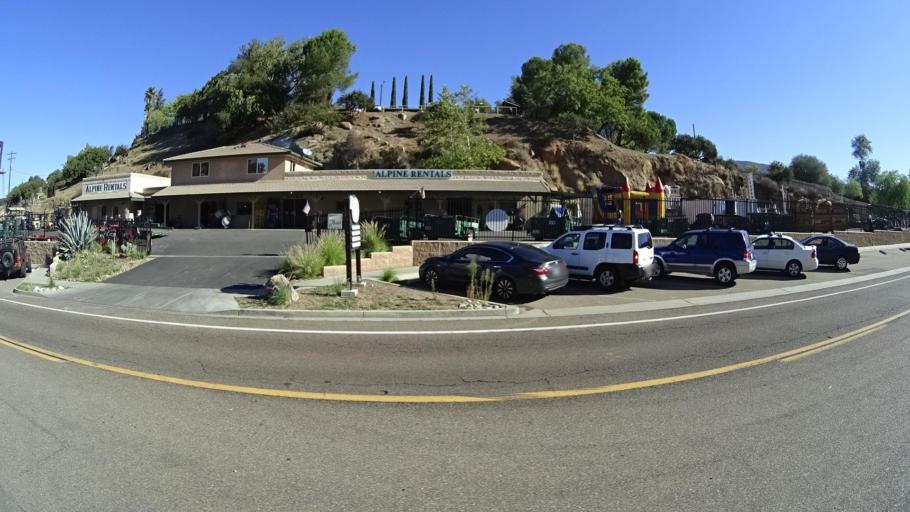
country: US
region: California
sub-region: San Diego County
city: Alpine
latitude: 32.8359
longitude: -116.7691
